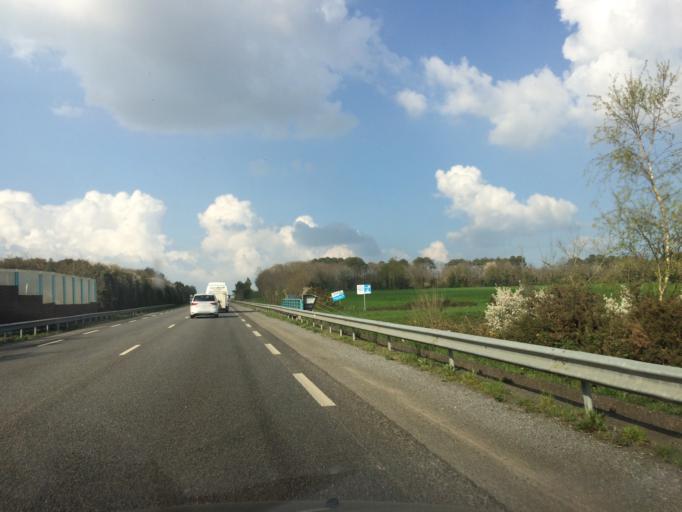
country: FR
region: Pays de la Loire
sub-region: Departement de la Loire-Atlantique
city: Saint-Nicolas-de-Redon
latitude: 47.6387
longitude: -2.0523
